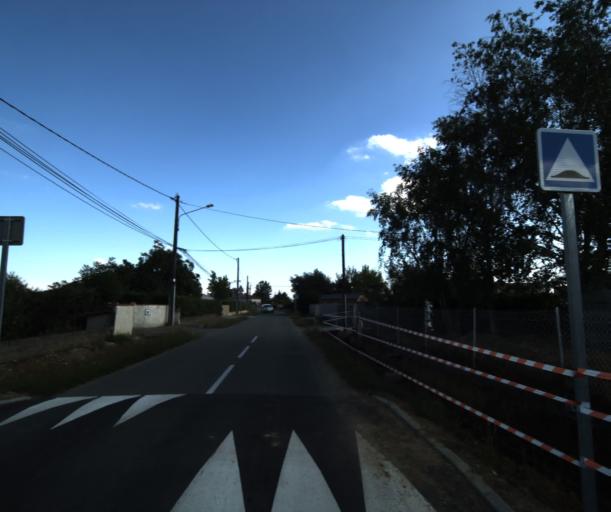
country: FR
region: Midi-Pyrenees
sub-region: Departement de la Haute-Garonne
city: Saint-Lys
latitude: 43.4996
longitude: 1.1911
